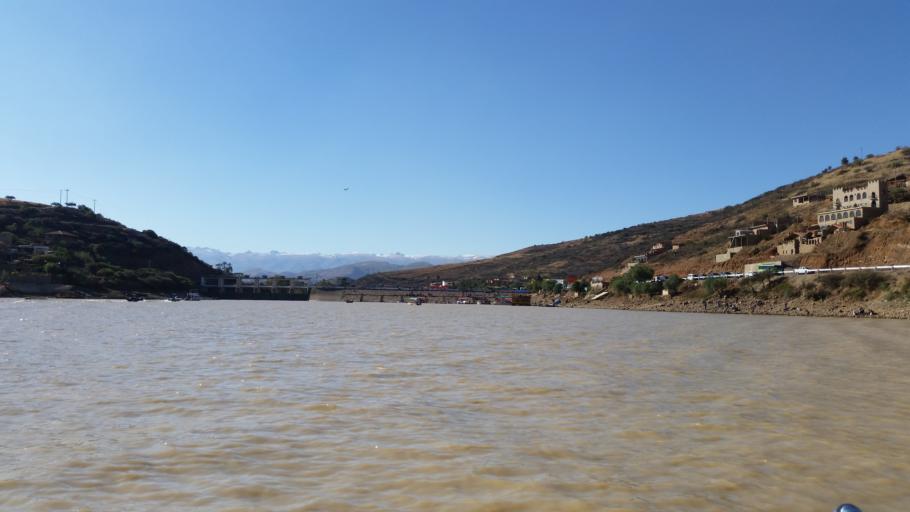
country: BO
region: Cochabamba
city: Tarata
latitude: -17.5320
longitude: -66.0858
